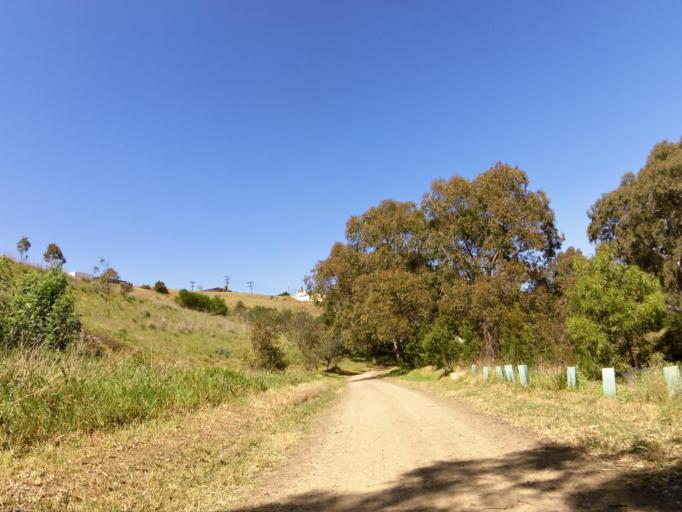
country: AU
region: Victoria
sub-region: Brimbank
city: Albion
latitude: -37.7638
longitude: 144.8544
